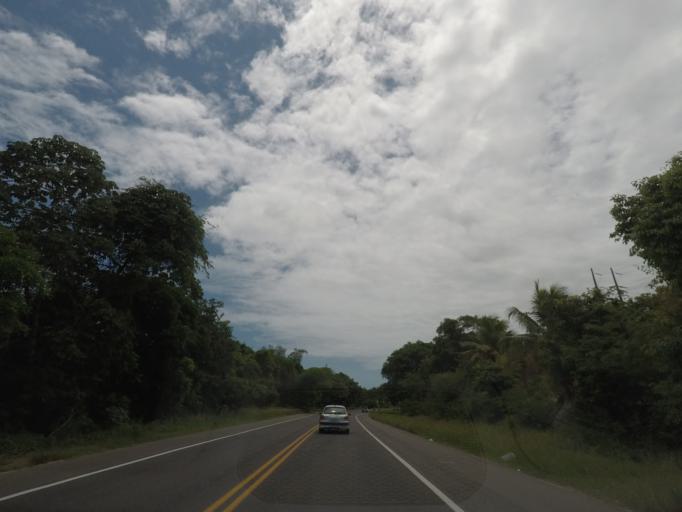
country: BR
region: Bahia
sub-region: Itaparica
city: Itaparica
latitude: -12.9586
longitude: -38.6325
